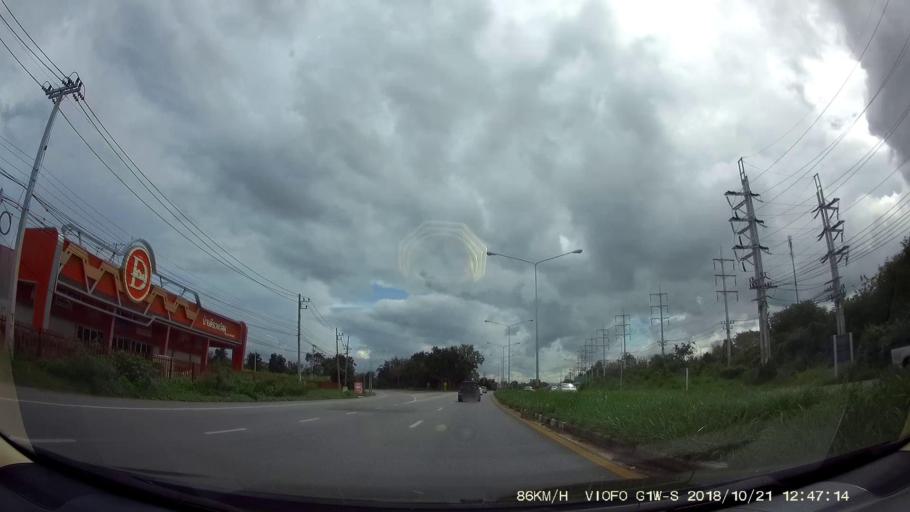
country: TH
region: Nakhon Ratchasima
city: Amphoe Sikhiu
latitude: 14.9312
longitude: 101.6831
